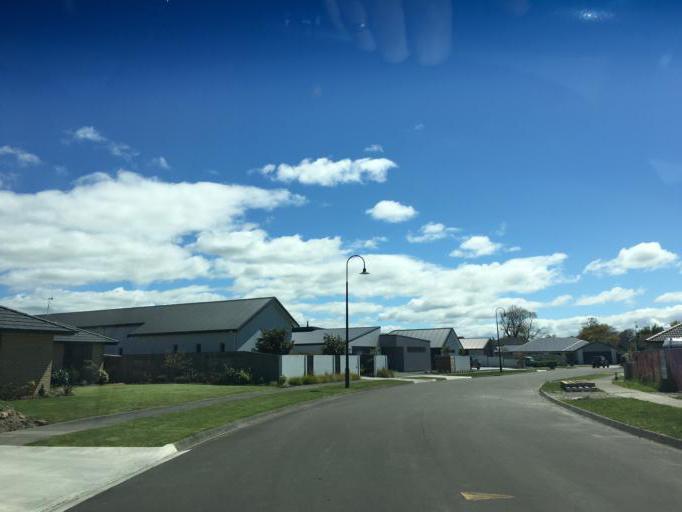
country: NZ
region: Manawatu-Wanganui
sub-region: Palmerston North City
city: Palmerston North
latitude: -40.3796
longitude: 175.5753
